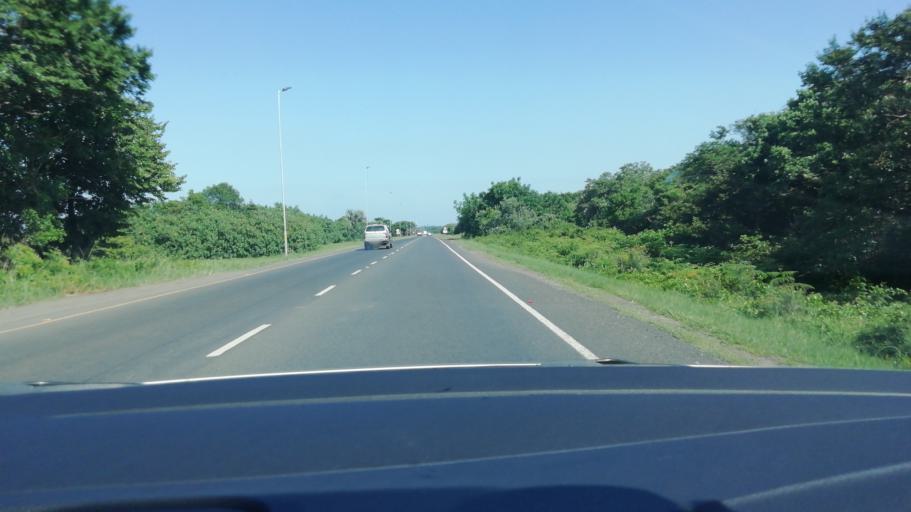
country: ZA
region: KwaZulu-Natal
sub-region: uThungulu District Municipality
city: Richards Bay
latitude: -28.7830
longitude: 32.0843
